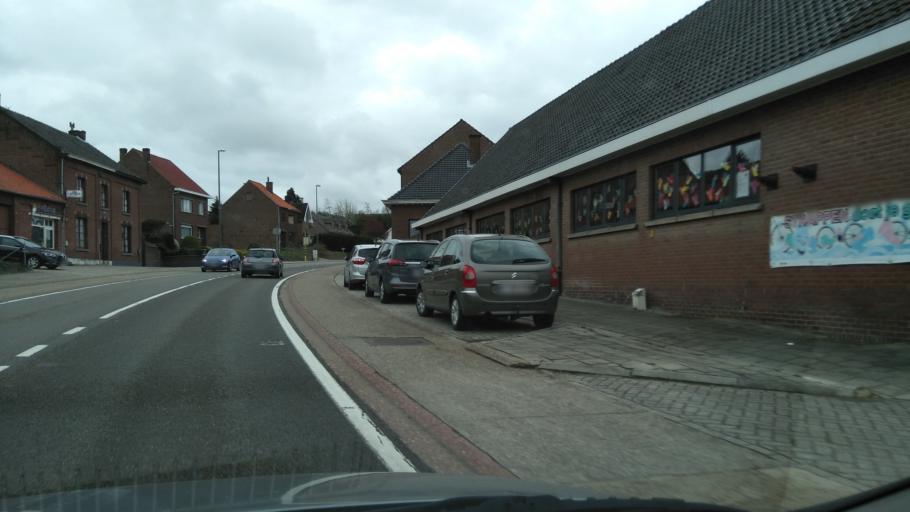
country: BE
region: Flanders
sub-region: Provincie Limburg
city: Bilzen
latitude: 50.8429
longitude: 5.5499
